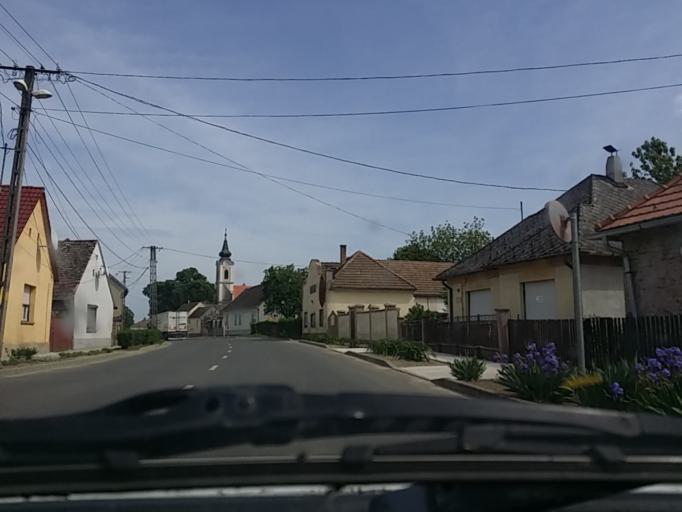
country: HU
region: Baranya
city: Vajszlo
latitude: 45.8605
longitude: 17.9807
